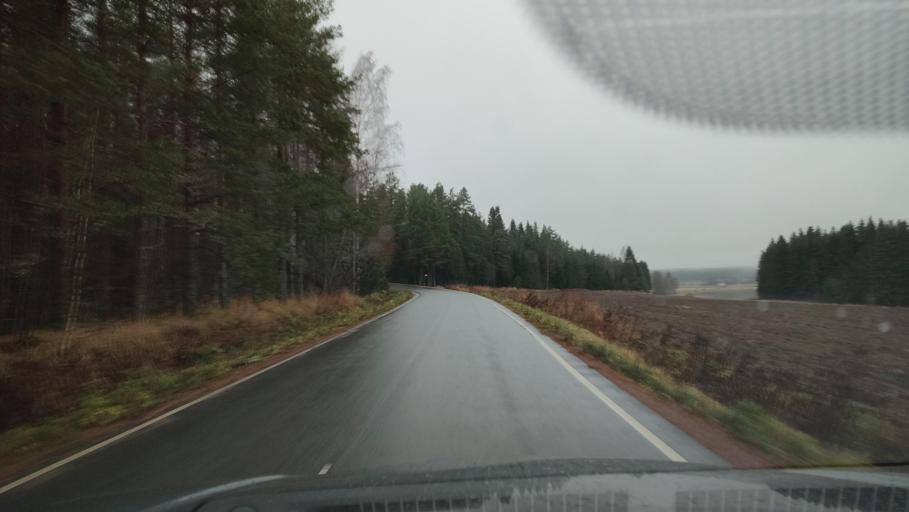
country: FI
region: Southern Ostrobothnia
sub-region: Suupohja
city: Karijoki
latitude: 62.1346
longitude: 21.6731
